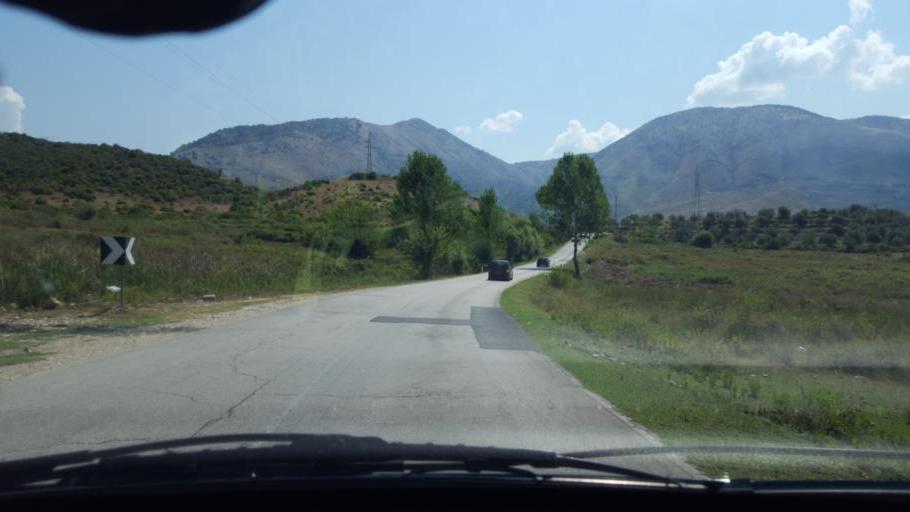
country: AL
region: Vlore
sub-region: Rrethi i Delvines
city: Mesopotam
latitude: 39.9120
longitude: 20.1133
